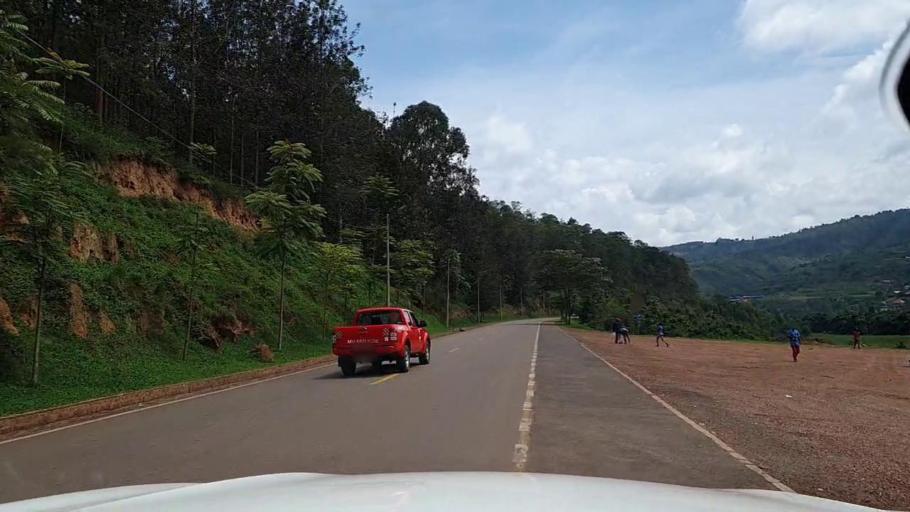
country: RW
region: Kigali
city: Kigali
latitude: -1.8612
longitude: 30.0897
